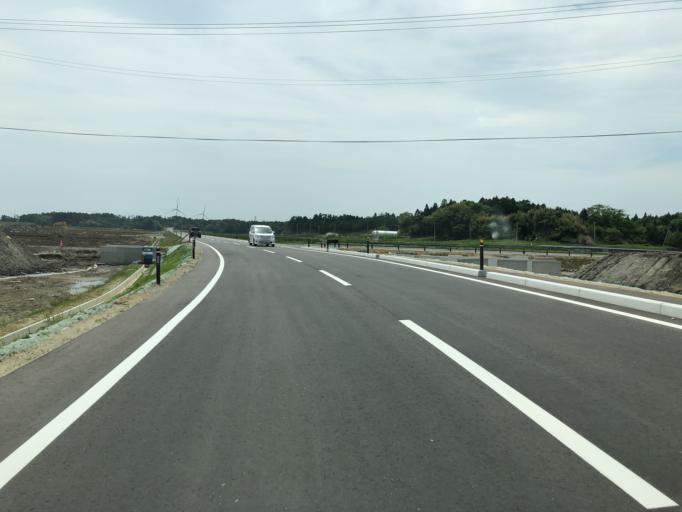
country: JP
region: Fukushima
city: Namie
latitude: 37.7212
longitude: 141.0028
